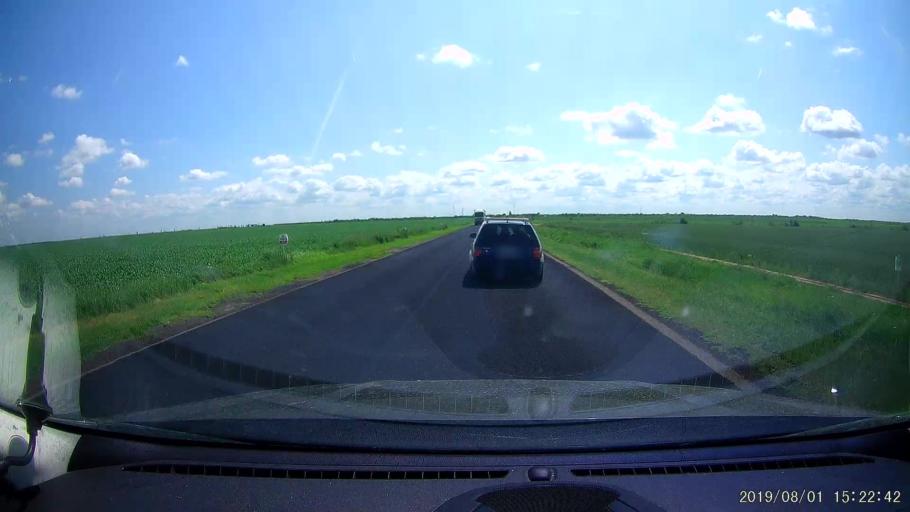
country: RO
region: Braila
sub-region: Comuna Viziru
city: Lanurile
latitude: 45.0504
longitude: 27.7723
